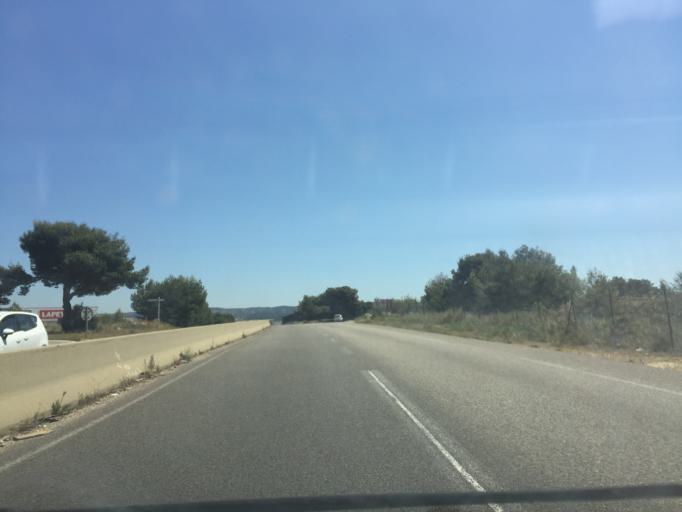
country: FR
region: Provence-Alpes-Cote d'Azur
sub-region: Departement des Bouches-du-Rhone
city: Vitrolles
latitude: 43.4442
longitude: 5.2406
